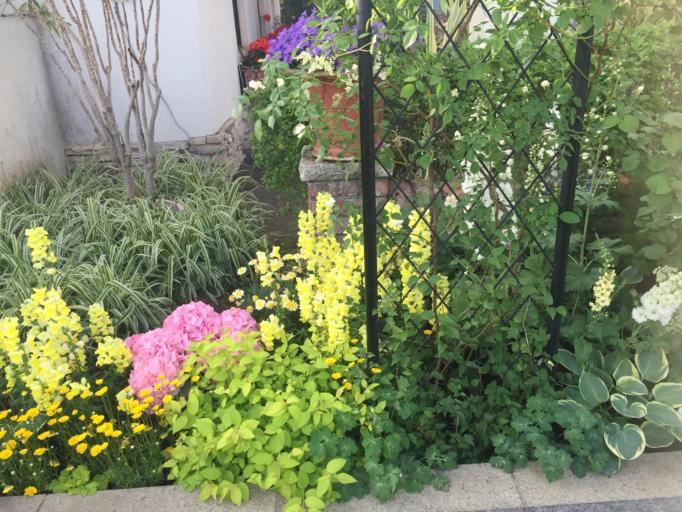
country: JP
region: Shizuoka
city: Kosai-shi
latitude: 34.7631
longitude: 137.6328
